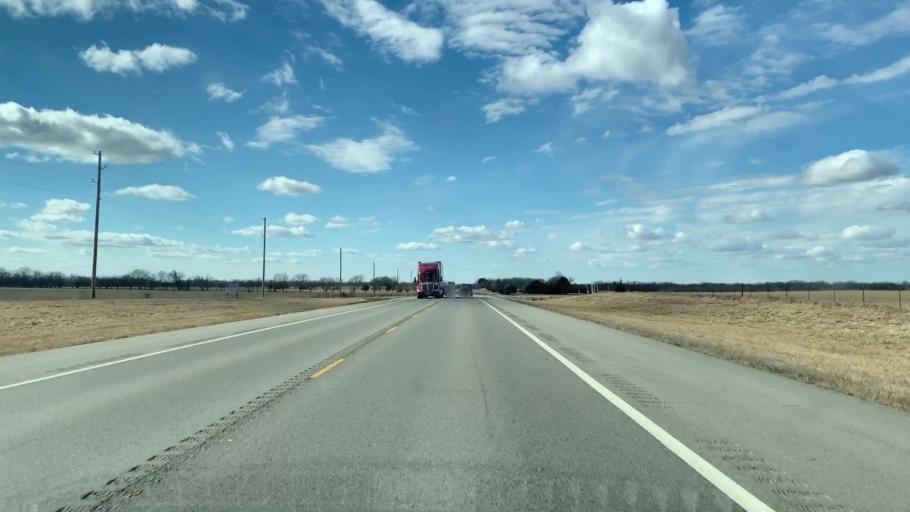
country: US
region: Kansas
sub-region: Labette County
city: Oswego
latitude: 37.3401
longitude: -95.0478
